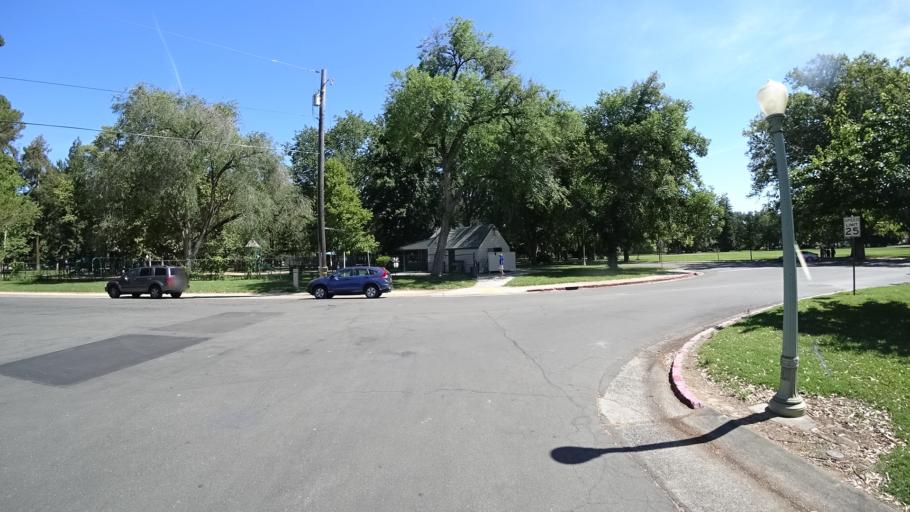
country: US
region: California
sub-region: Sacramento County
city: Sacramento
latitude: 38.5444
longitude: -121.5033
